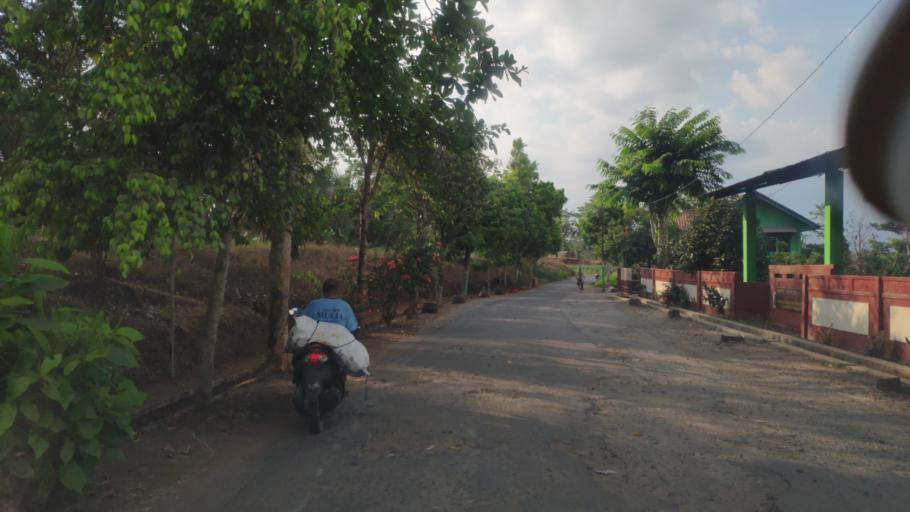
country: ID
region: Central Java
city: Gombong
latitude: -7.4139
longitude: 109.6223
